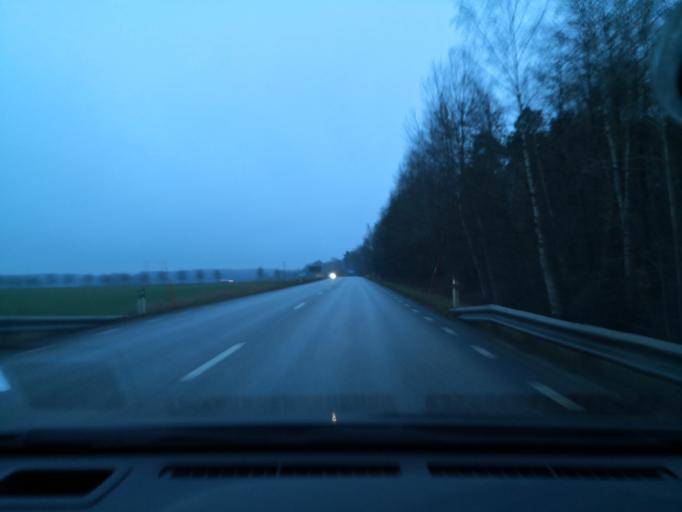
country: SE
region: Soedermanland
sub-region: Eskilstuna Kommun
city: Skogstorp
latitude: 59.3183
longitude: 16.4552
